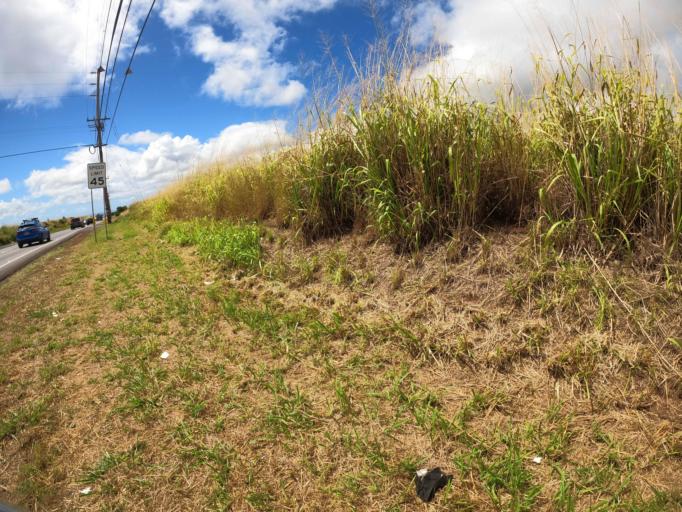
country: US
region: Hawaii
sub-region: Honolulu County
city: Village Park
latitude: 21.4165
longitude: -158.0469
